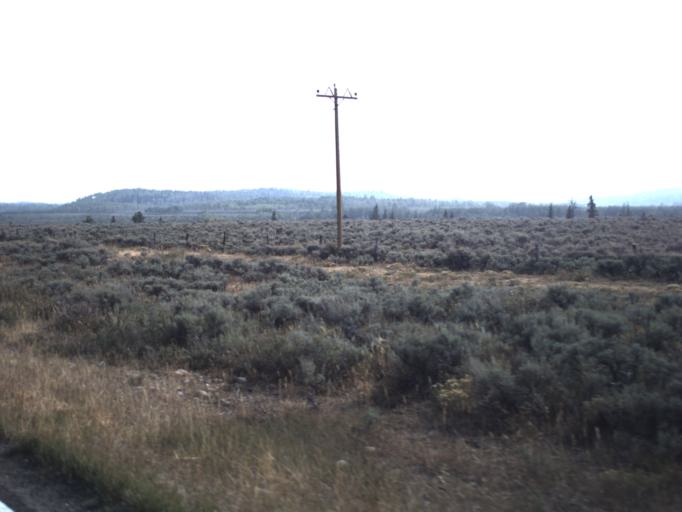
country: US
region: Wyoming
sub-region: Uinta County
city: Evanston
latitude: 40.9596
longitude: -110.8444
